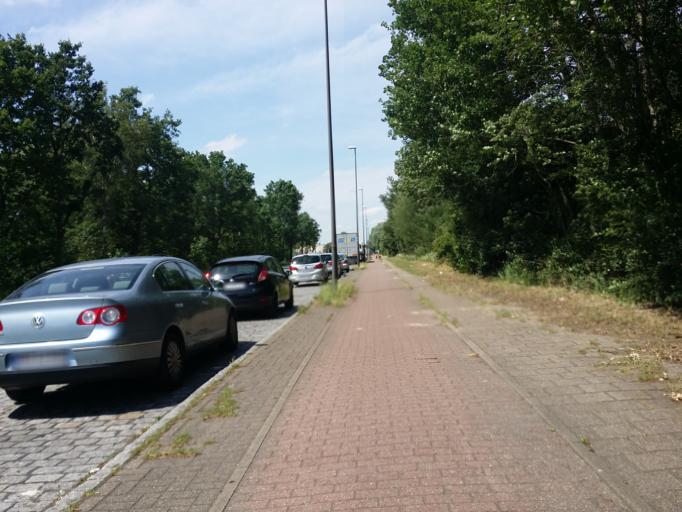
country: DE
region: Lower Saxony
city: Stuhr
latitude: 53.0821
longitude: 8.7526
